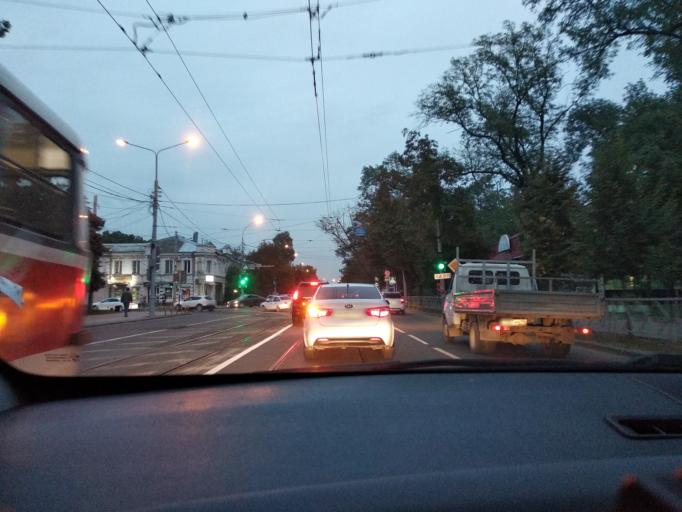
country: RU
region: Krasnodarskiy
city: Krasnodar
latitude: 45.0143
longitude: 38.9707
